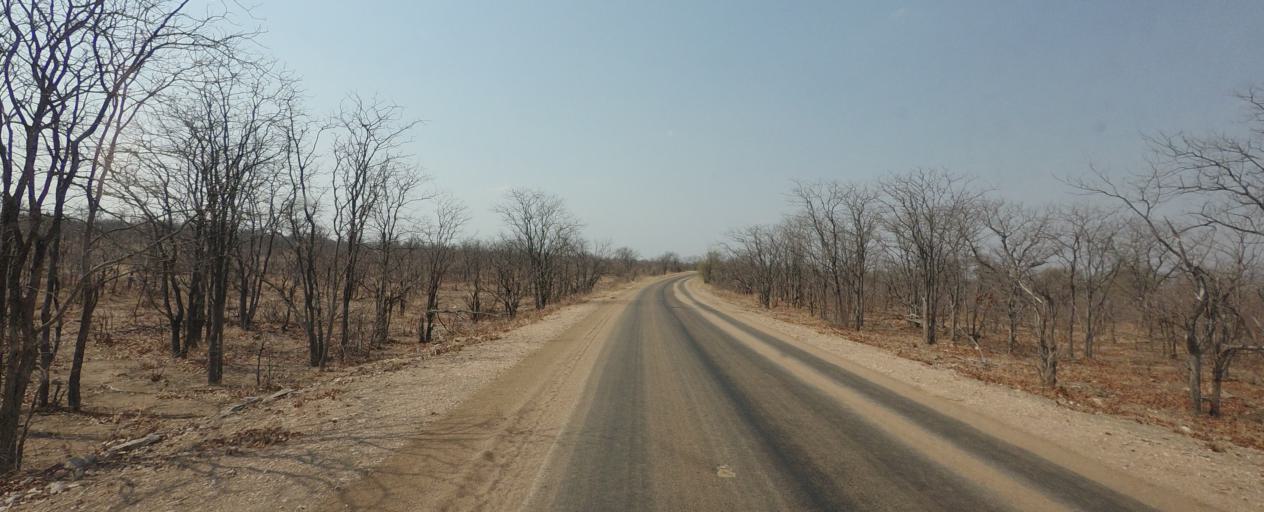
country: ZA
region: Limpopo
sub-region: Mopani District Municipality
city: Giyani
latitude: -23.2002
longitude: 31.3077
